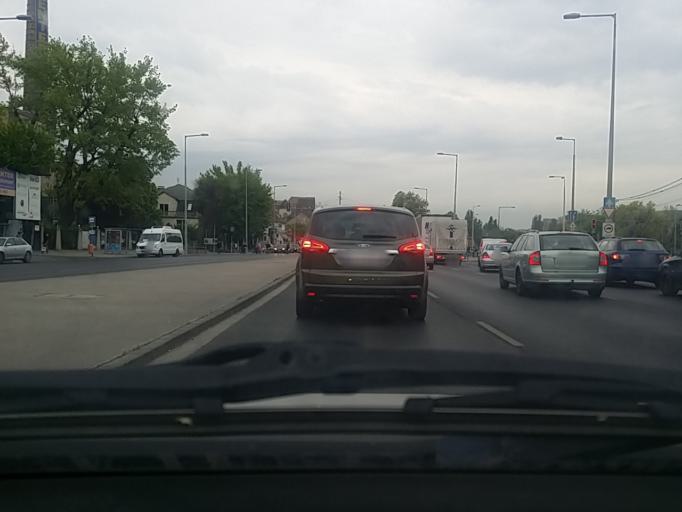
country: HU
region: Budapest
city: Budapest III. keruelet
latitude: 47.5576
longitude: 19.0460
